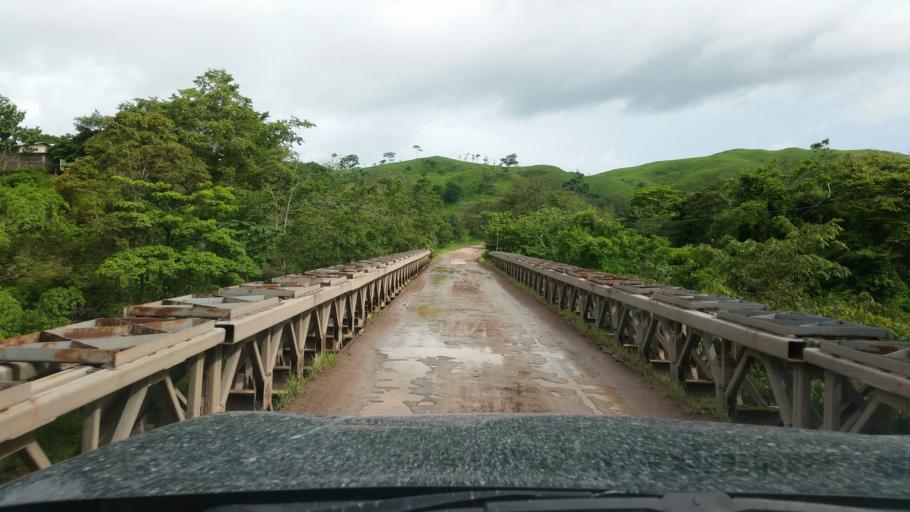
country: NI
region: Atlantico Norte (RAAN)
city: Siuna
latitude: 13.5284
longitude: -84.8230
